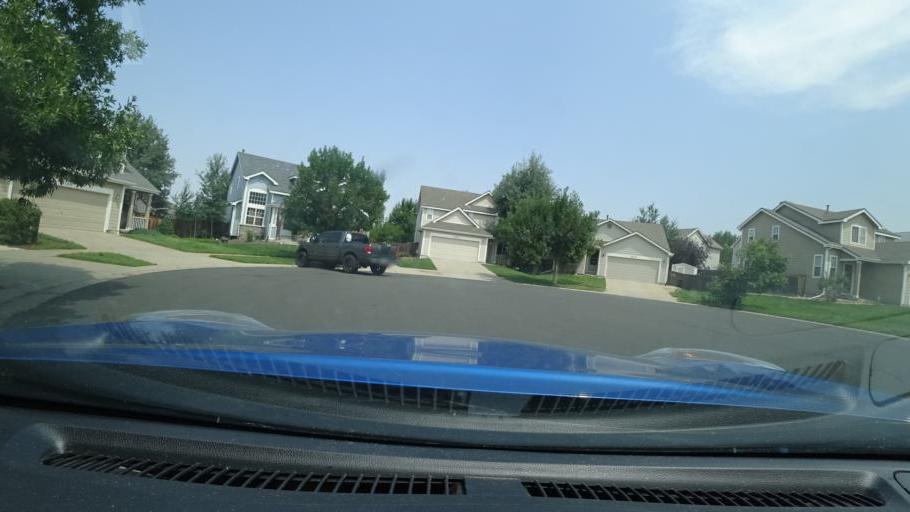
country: US
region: Colorado
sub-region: Adams County
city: Aurora
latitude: 39.7721
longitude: -104.7427
